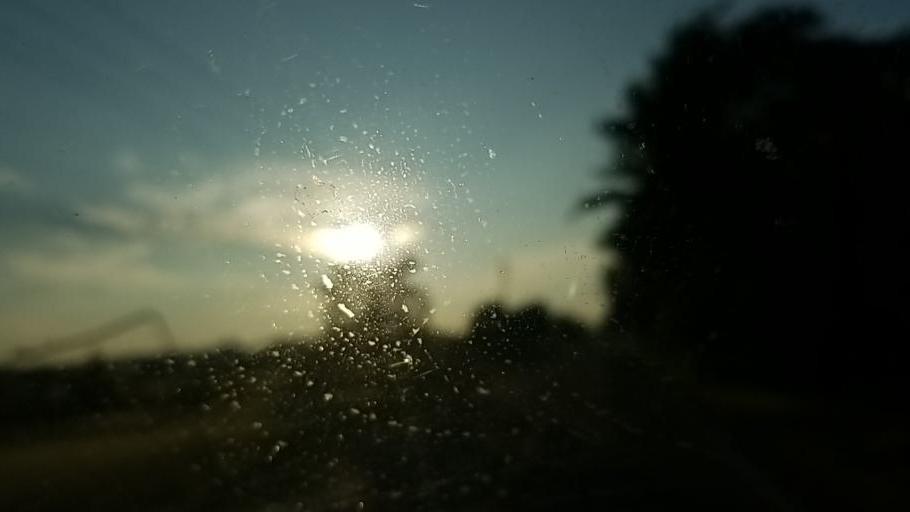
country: US
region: Michigan
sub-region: Montcalm County
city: Lakeview
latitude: 43.3592
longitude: -85.3272
